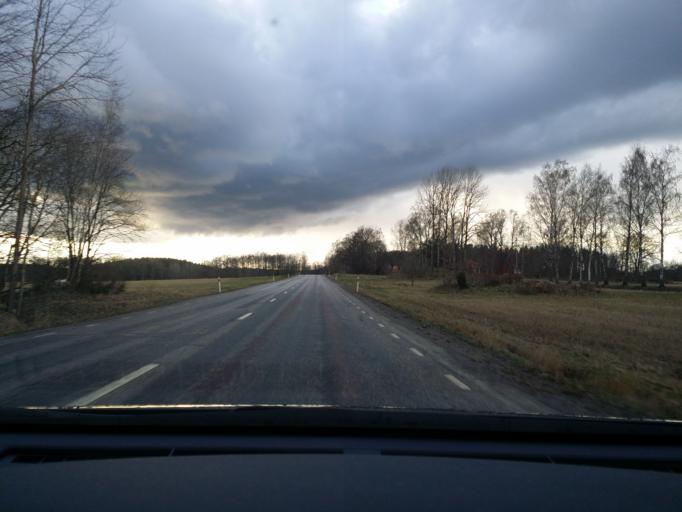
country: SE
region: Soedermanland
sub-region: Eskilstuna Kommun
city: Arla
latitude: 59.3850
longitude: 16.6620
